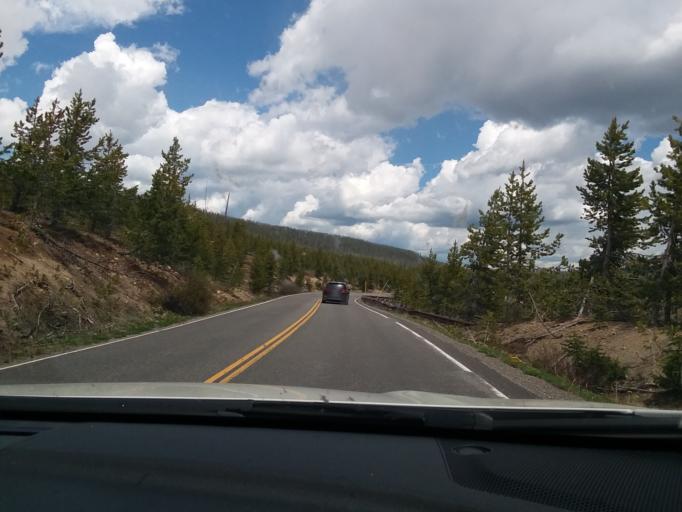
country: US
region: Montana
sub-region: Gallatin County
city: West Yellowstone
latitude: 44.2188
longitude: -110.6564
